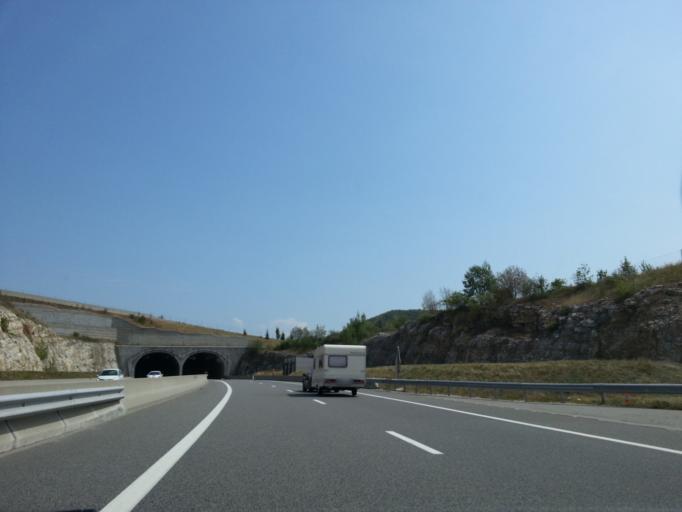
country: FR
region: Rhone-Alpes
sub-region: Departement de la Haute-Savoie
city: Cruseilles
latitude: 46.0183
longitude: 6.1010
